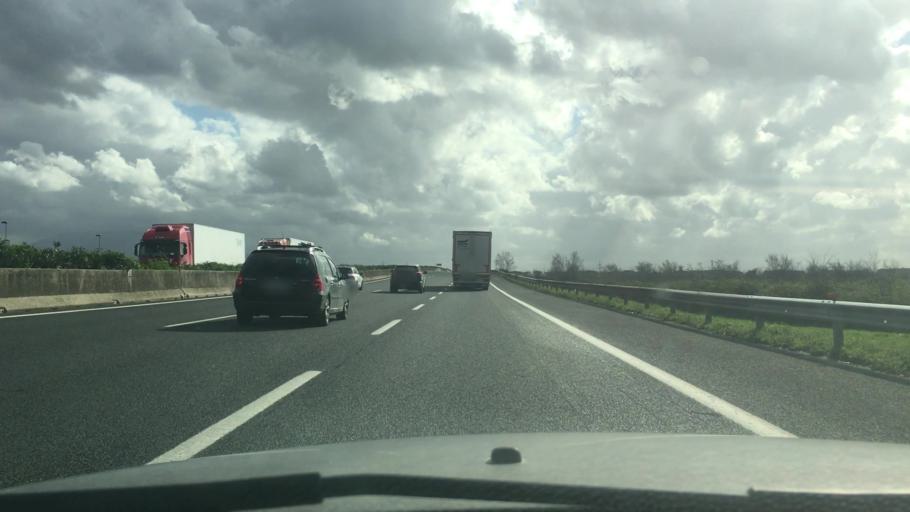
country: IT
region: Campania
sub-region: Provincia di Napoli
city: Pascarola
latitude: 41.0039
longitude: 14.3235
